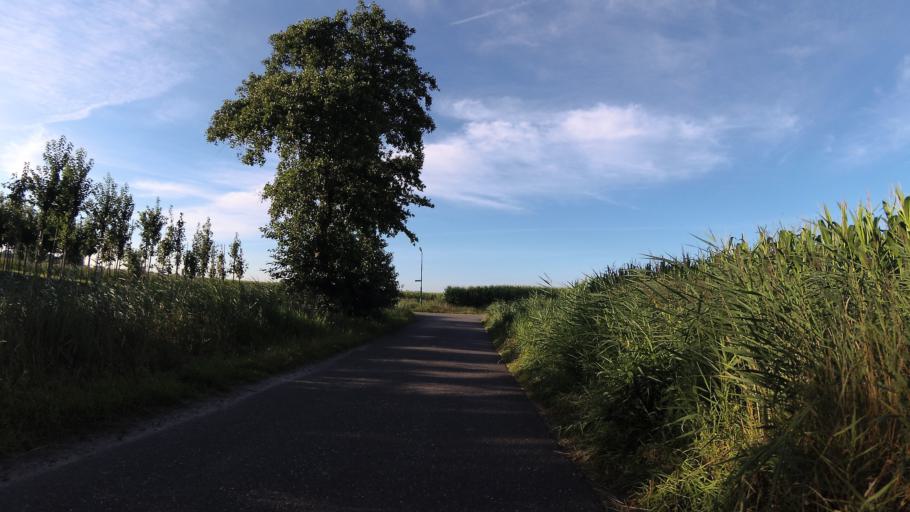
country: NL
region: North Brabant
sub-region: Gemeente Breda
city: Hoge Vucht
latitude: 51.6197
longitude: 4.8051
